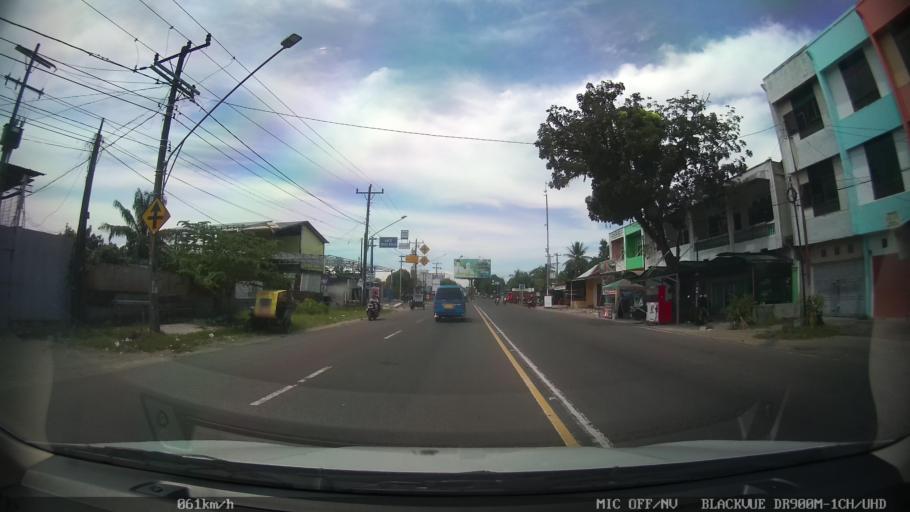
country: ID
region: North Sumatra
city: Binjai
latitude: 3.6205
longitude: 98.5018
